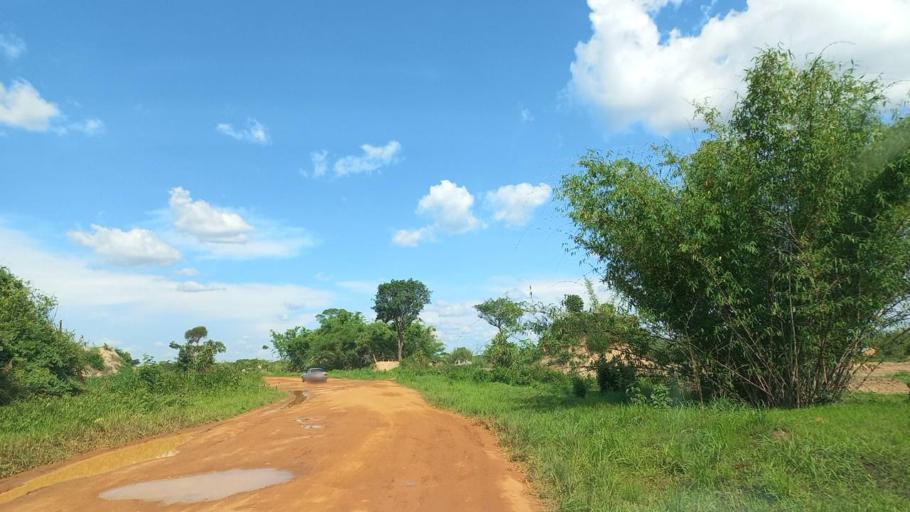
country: ZM
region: Copperbelt
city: Kitwe
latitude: -12.8636
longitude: 28.3799
